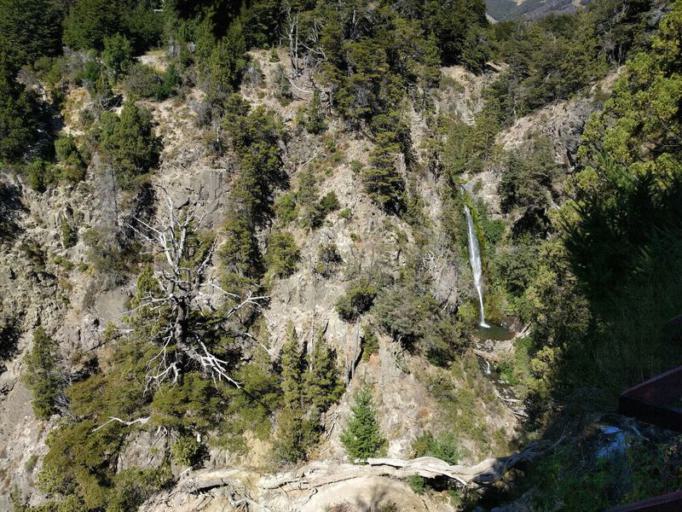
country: AR
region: Neuquen
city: Villa La Angostura
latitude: -40.6629
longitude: -71.4020
